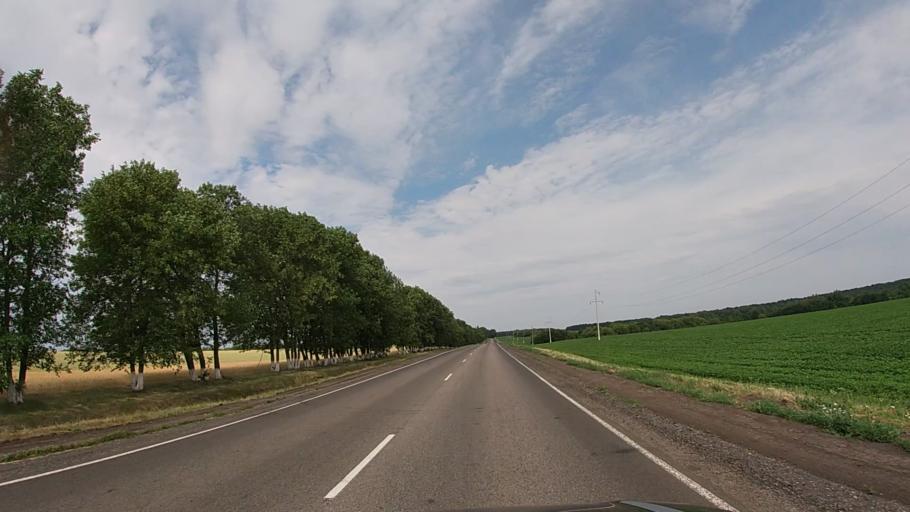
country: RU
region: Belgorod
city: Krasnaya Yaruga
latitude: 50.8092
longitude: 35.5233
